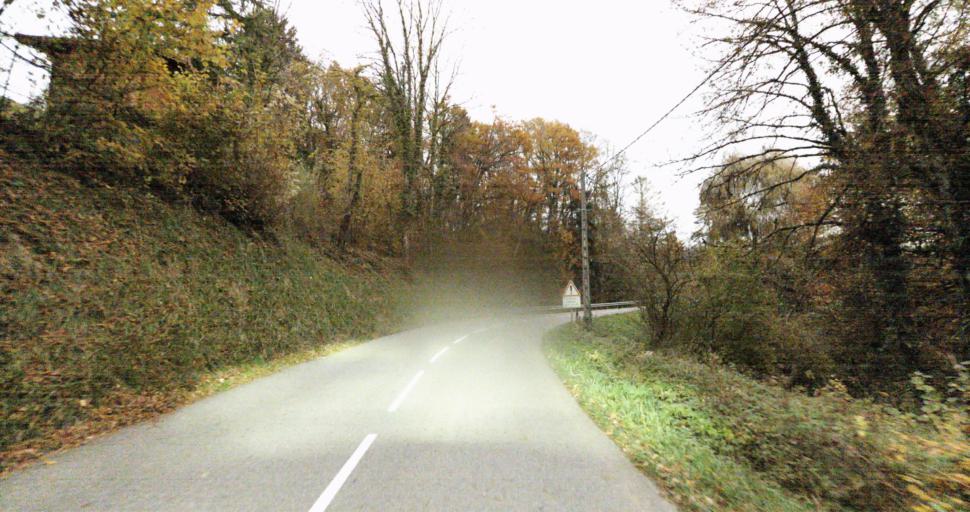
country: FR
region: Rhone-Alpes
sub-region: Departement de la Haute-Savoie
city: Alby-sur-Cheran
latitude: 45.8420
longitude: 6.0029
